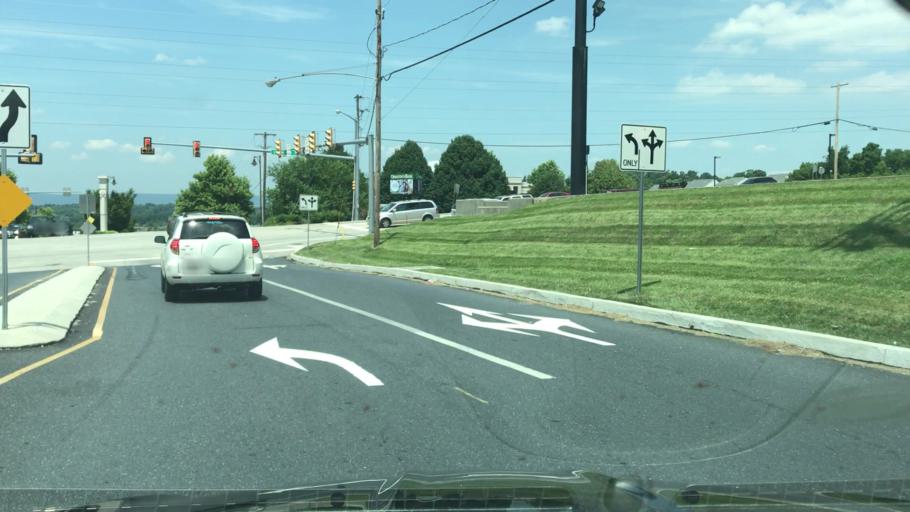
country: US
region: Pennsylvania
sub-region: Dauphin County
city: Lawnton
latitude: 40.2426
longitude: -76.8018
